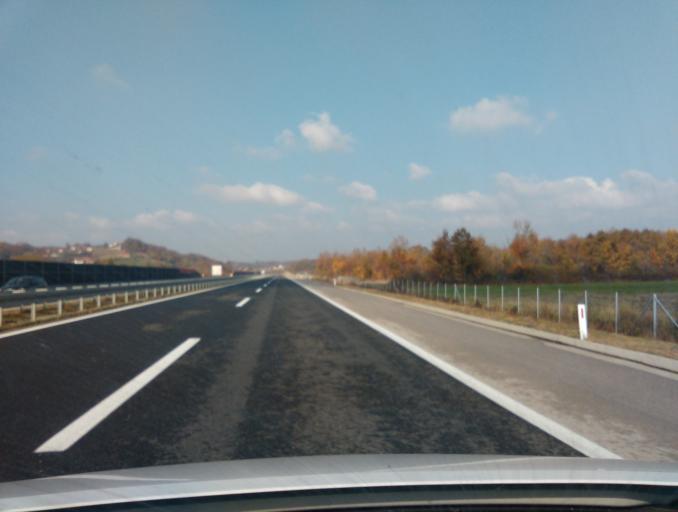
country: BA
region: Republika Srpska
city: Doboj
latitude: 44.8212
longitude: 18.0257
